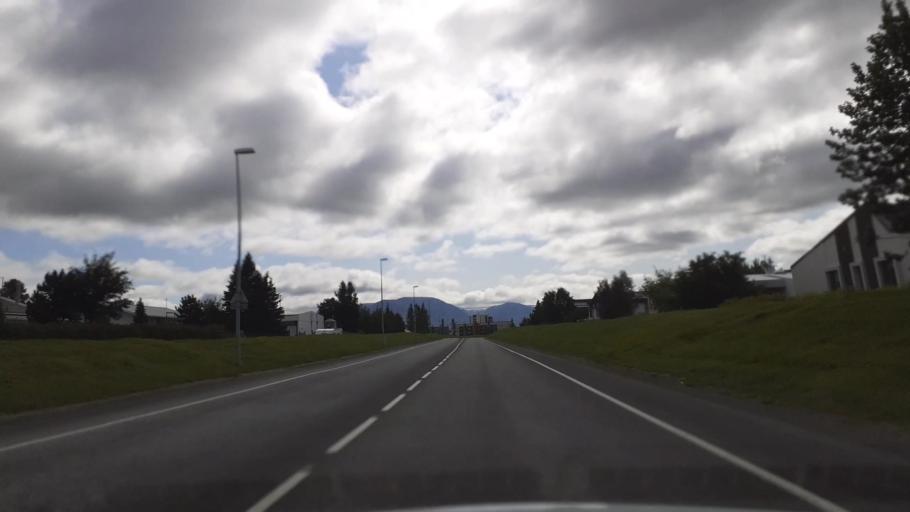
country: IS
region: Northeast
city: Akureyri
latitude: 65.6733
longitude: -18.1090
